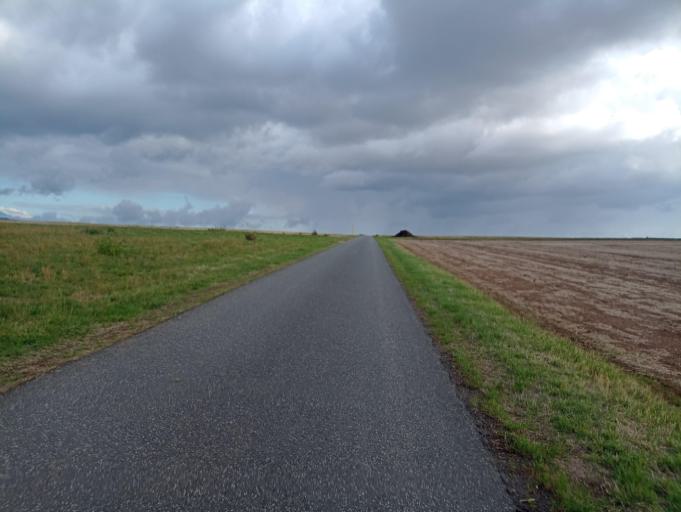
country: DE
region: Hesse
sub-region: Regierungsbezirk Darmstadt
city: Bad Homburg vor der Hoehe
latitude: 50.1960
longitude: 8.6257
